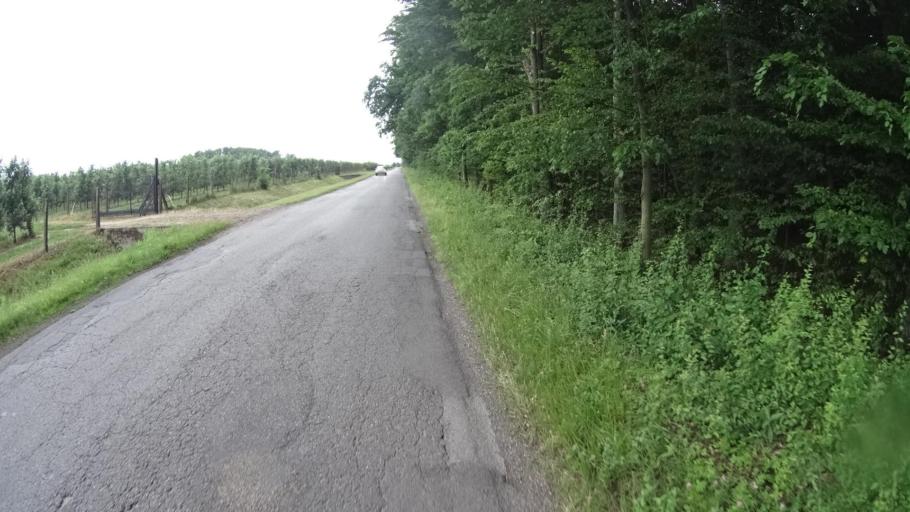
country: PL
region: Masovian Voivodeship
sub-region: Powiat grojecki
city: Goszczyn
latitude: 51.7793
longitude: 20.8537
